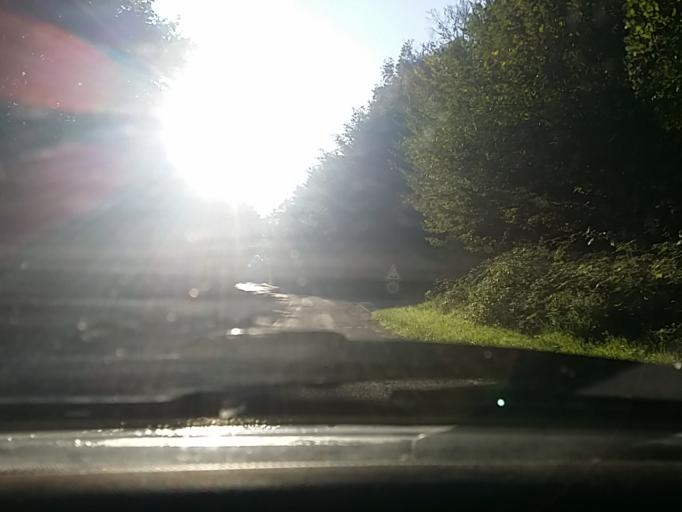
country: HU
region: Pest
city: Visegrad
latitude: 47.7355
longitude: 18.9533
